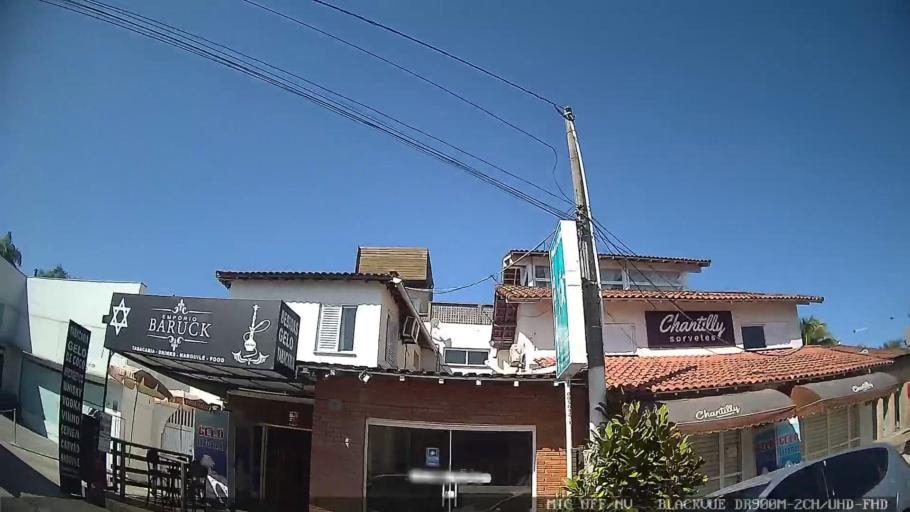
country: BR
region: Sao Paulo
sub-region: Guaruja
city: Guaruja
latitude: -23.9878
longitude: -46.2045
